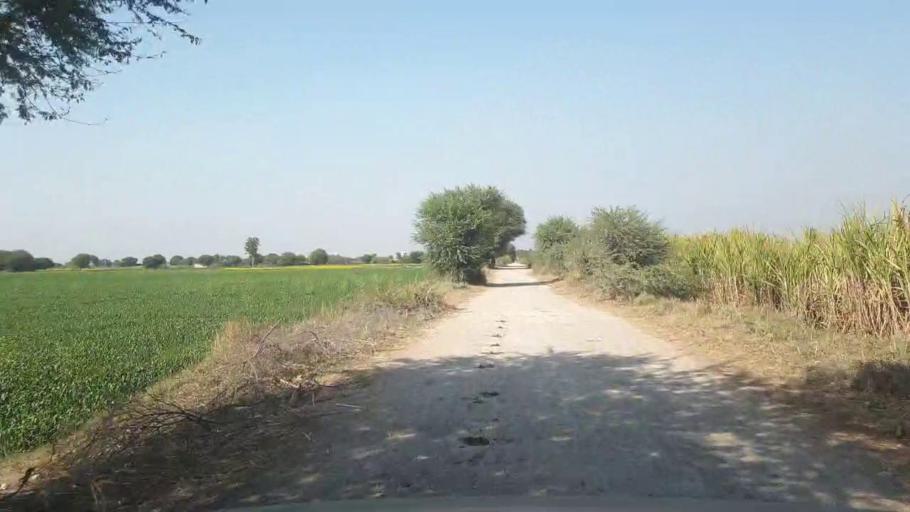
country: PK
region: Sindh
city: Chambar
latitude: 25.3035
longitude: 68.8457
